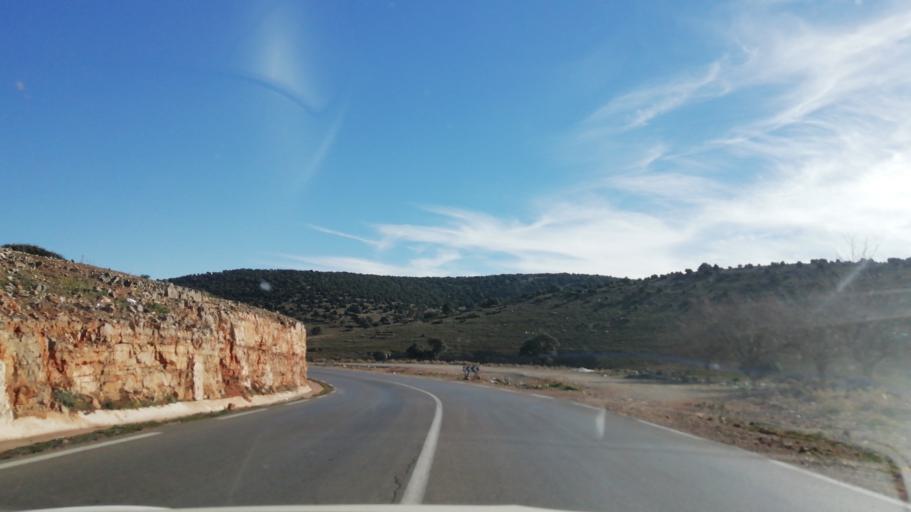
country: DZ
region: Tlemcen
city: Sebdou
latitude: 34.7172
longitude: -1.3365
